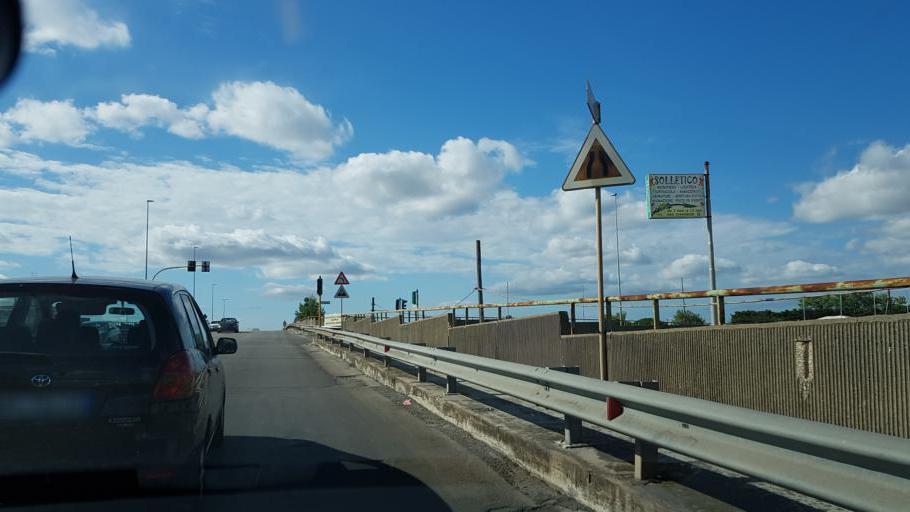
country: IT
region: Apulia
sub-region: Provincia di Lecce
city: Lecce
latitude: 40.3549
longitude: 18.1518
